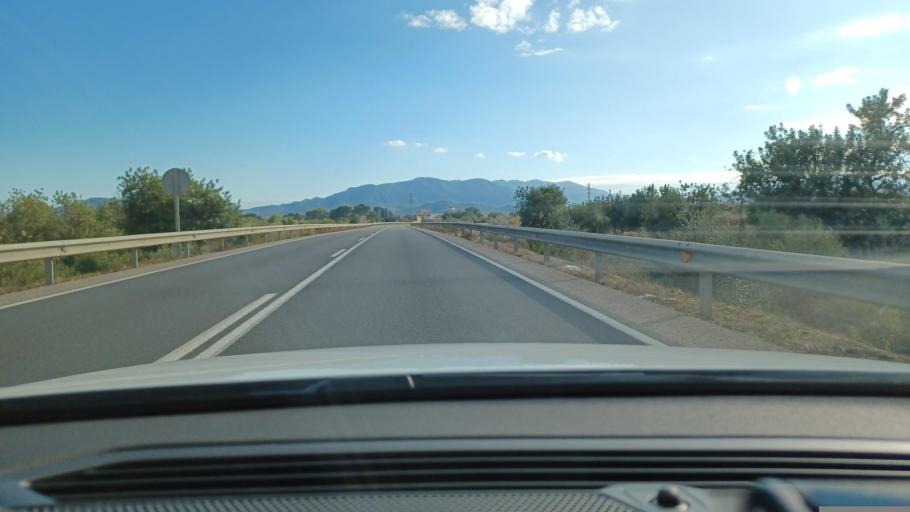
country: ES
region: Catalonia
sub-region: Provincia de Tarragona
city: Santa Barbara
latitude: 40.7216
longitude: 0.5046
